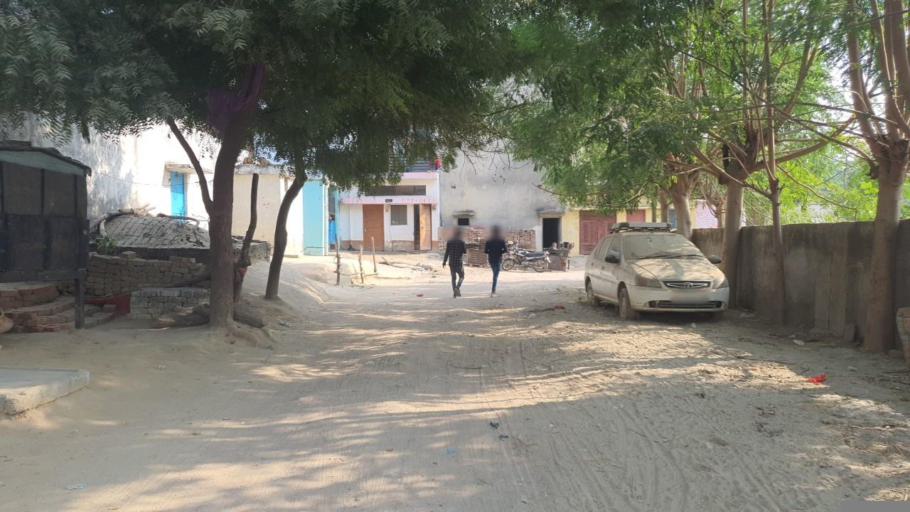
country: IN
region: Uttar Pradesh
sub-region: Lucknow District
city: Lucknow
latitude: 26.7992
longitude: 81.0049
